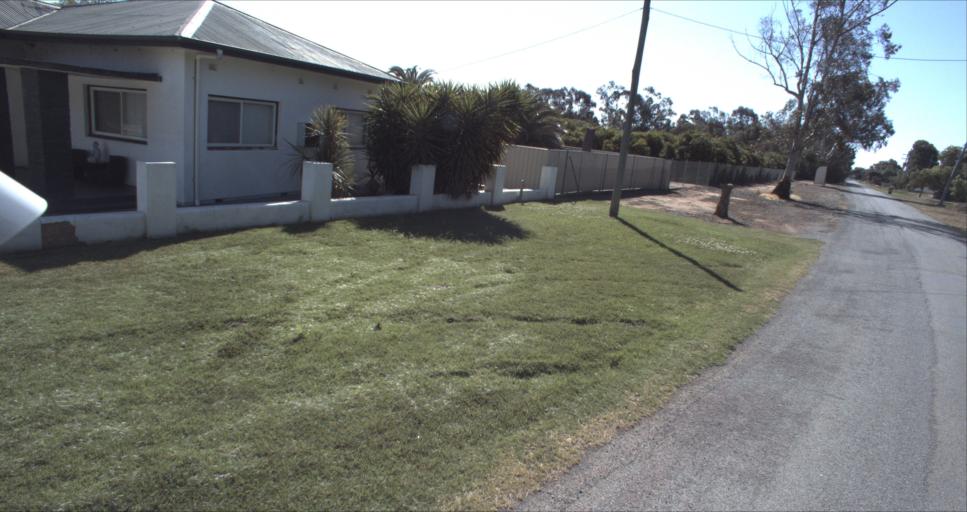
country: AU
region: New South Wales
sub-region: Leeton
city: Leeton
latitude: -34.5585
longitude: 146.3881
